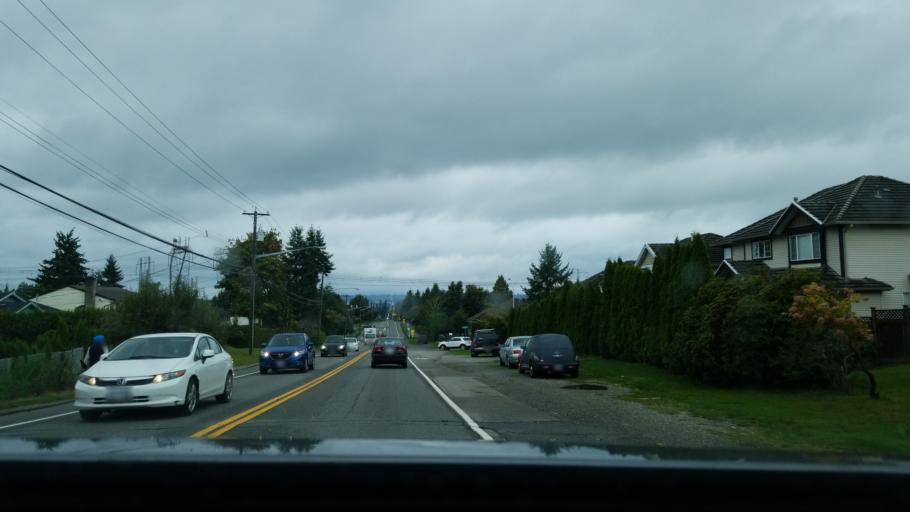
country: CA
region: British Columbia
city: Langley
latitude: 49.1188
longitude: -122.7156
